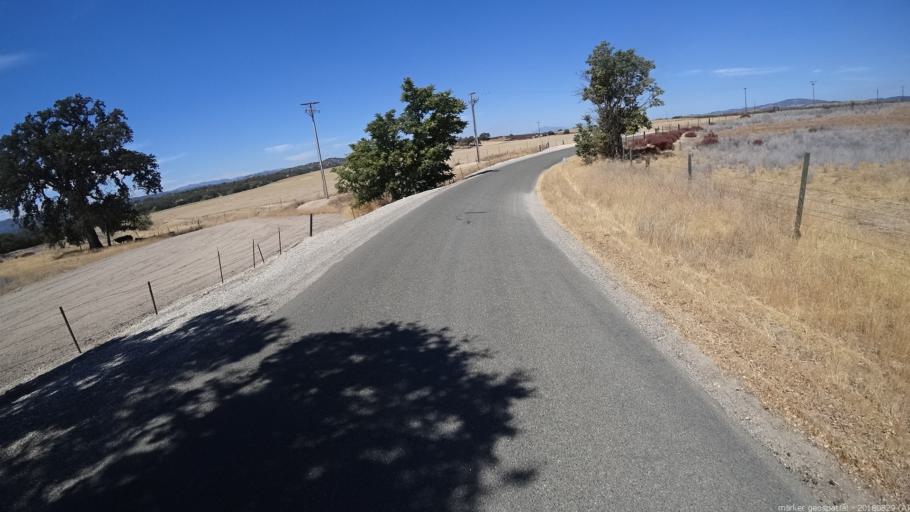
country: US
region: California
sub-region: San Luis Obispo County
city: Lake Nacimiento
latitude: 35.9081
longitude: -121.0376
